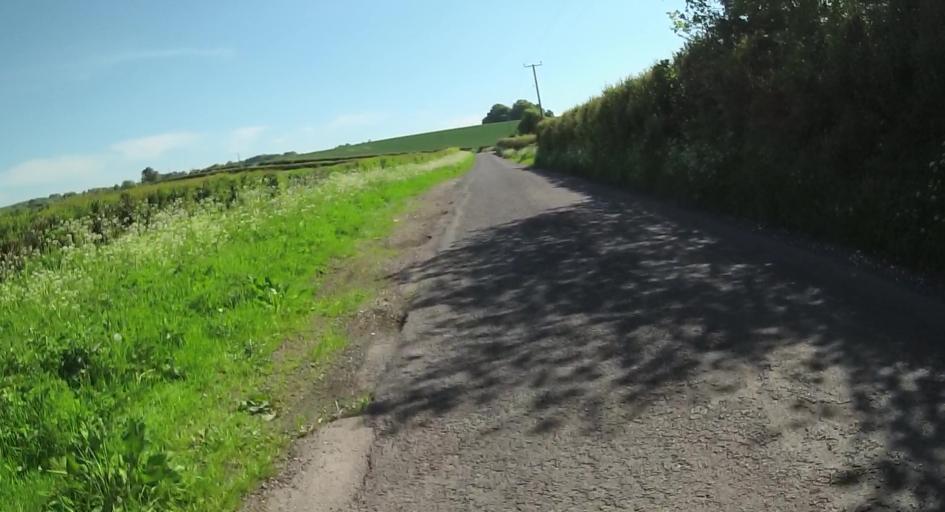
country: GB
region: England
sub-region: Hampshire
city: Kings Worthy
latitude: 51.0736
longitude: -1.2704
